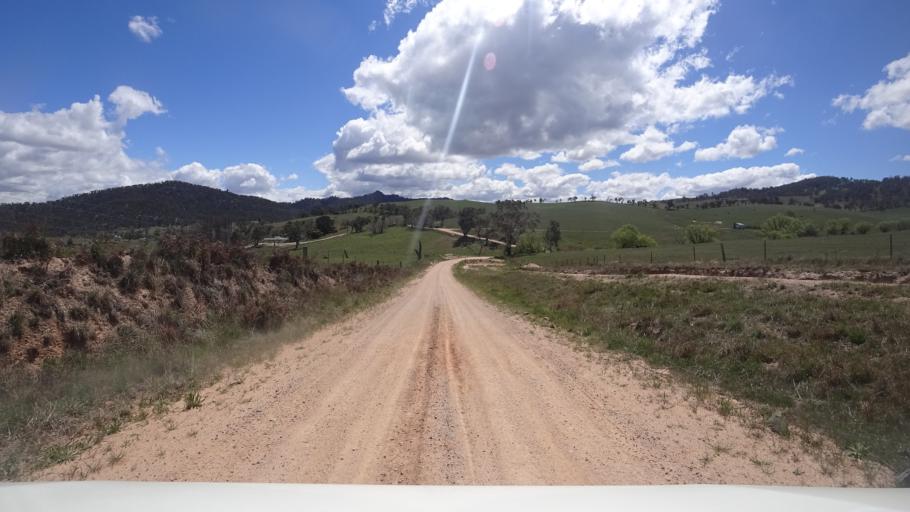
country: AU
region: New South Wales
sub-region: Oberon
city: Oberon
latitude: -33.5671
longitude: 149.9418
